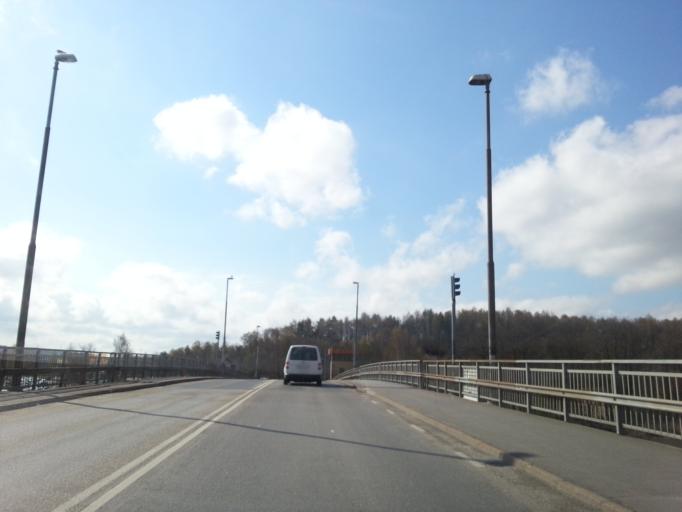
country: SE
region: Vaestra Goetaland
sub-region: Kungalvs Kommun
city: Kungalv
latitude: 57.8601
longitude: 11.9977
